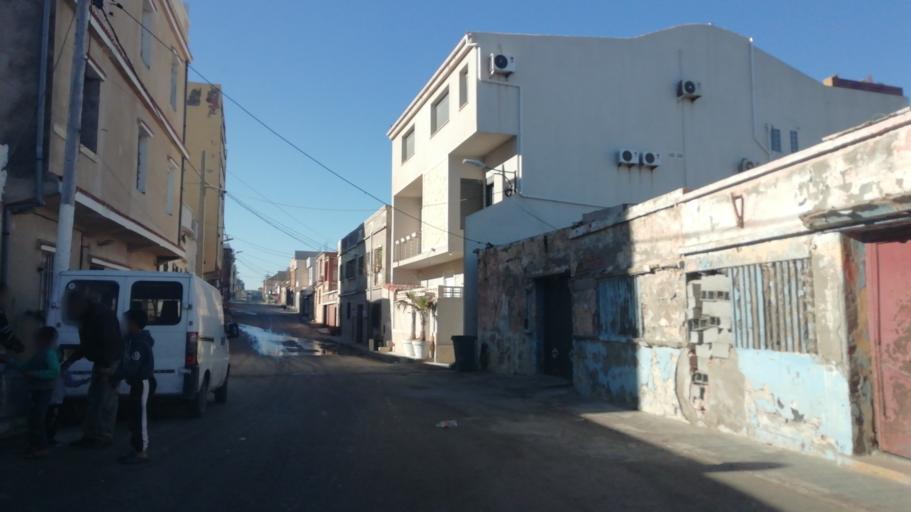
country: DZ
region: Oran
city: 'Ain el Turk
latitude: 35.7306
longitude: -0.8441
